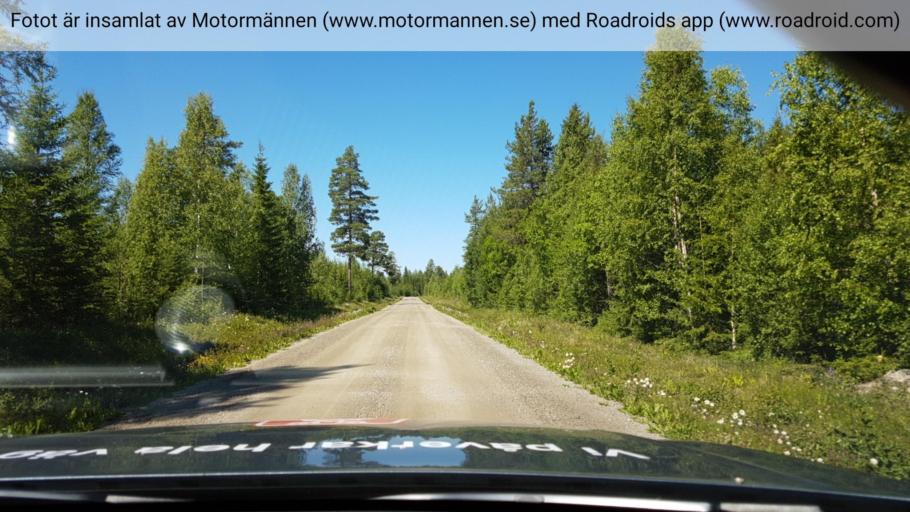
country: SE
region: Jaemtland
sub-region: Braecke Kommun
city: Braecke
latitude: 62.8015
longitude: 15.2374
